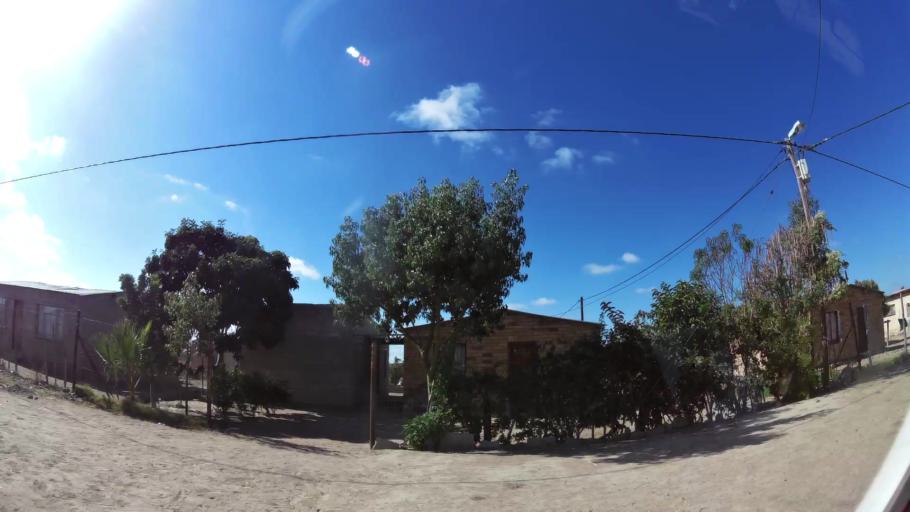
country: ZA
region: Limpopo
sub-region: Capricorn District Municipality
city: Polokwane
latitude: -23.8587
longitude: 29.3984
